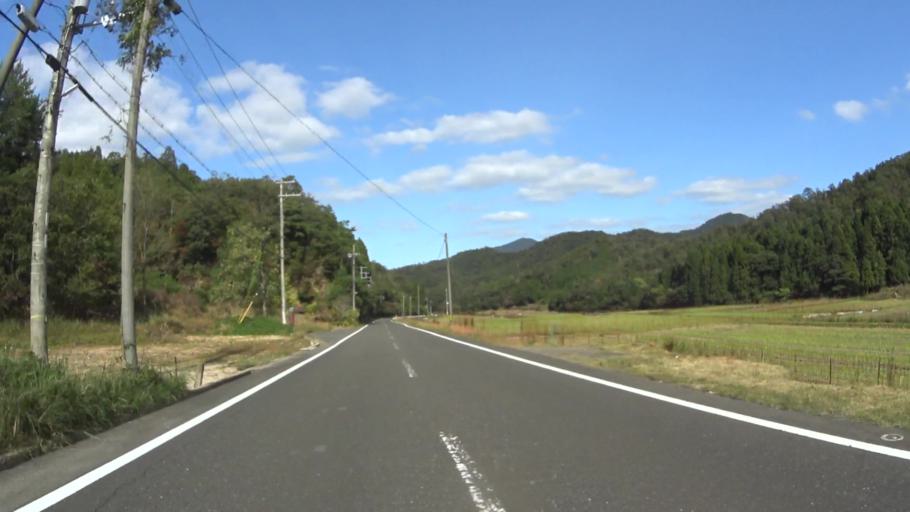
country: JP
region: Hyogo
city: Toyooka
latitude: 35.5536
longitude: 134.9773
